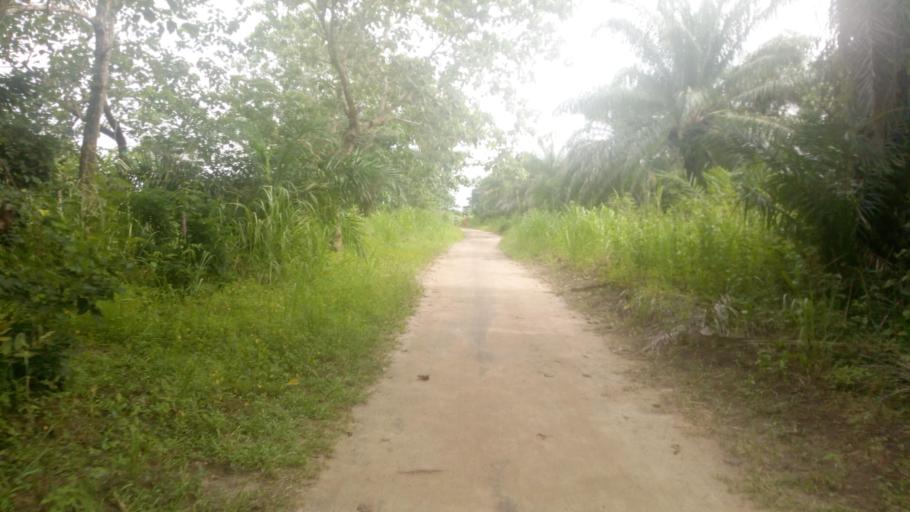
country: SL
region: Northern Province
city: Magburaka
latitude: 8.6748
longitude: -12.0321
